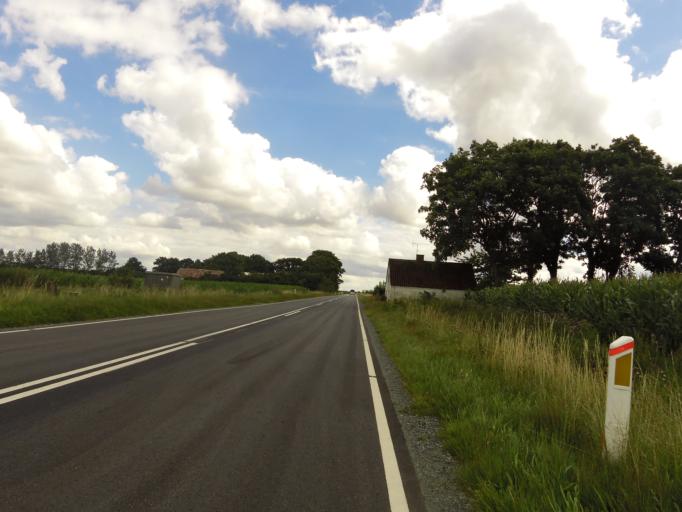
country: DK
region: South Denmark
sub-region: Haderslev Kommune
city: Vojens
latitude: 55.2789
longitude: 9.1857
